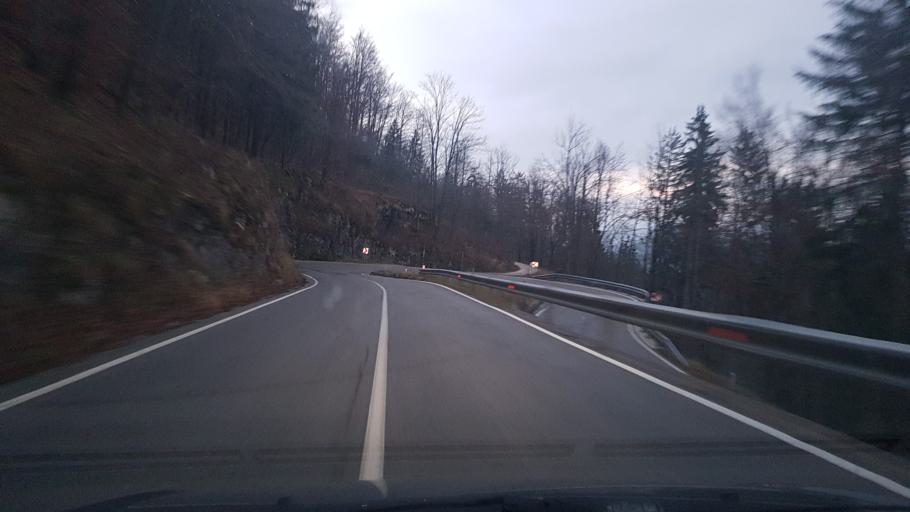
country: SI
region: Idrija
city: Idrija
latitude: 45.9541
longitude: 14.0763
